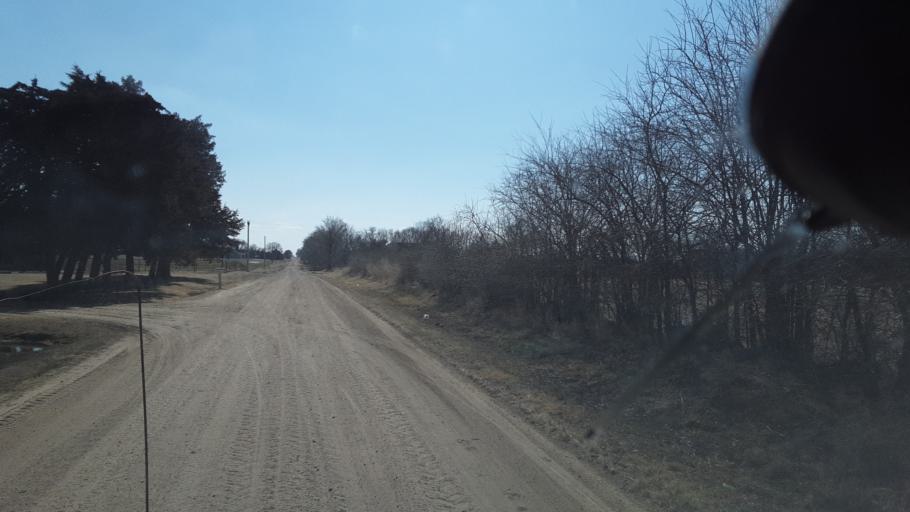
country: US
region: Kansas
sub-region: Reno County
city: Haven
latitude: 37.9138
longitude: -97.8484
